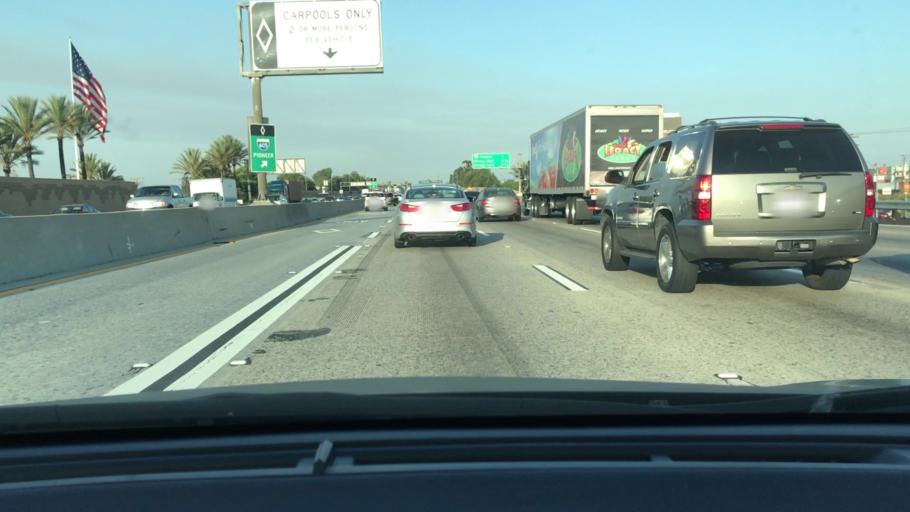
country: US
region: California
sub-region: Los Angeles County
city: Bellflower
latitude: 33.8759
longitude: -118.1267
